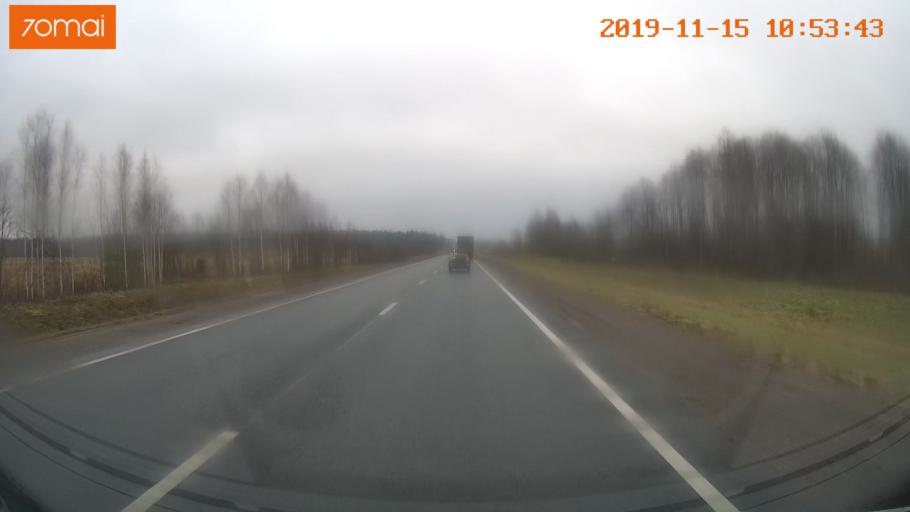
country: RU
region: Vologda
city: Chebsara
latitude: 59.1678
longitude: 38.7608
